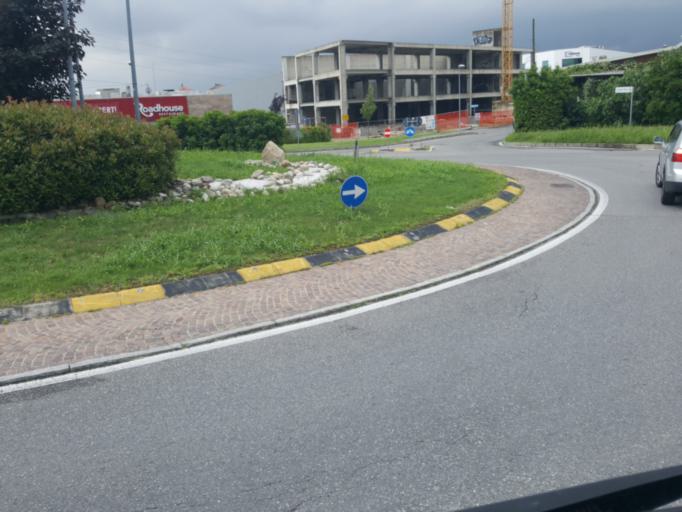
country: IT
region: Lombardy
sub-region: Provincia di Monza e Brianza
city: Giussano
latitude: 45.6809
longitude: 9.1958
